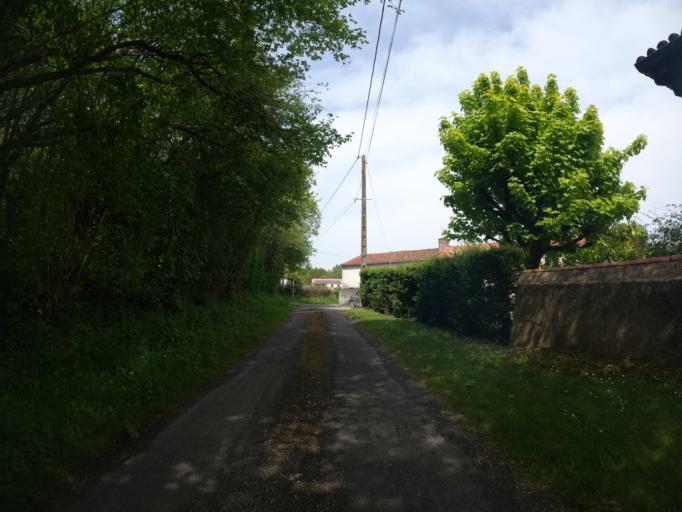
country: FR
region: Poitou-Charentes
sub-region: Departement des Deux-Sevres
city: La Chapelle-Saint-Laurent
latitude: 46.7616
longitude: -0.4659
